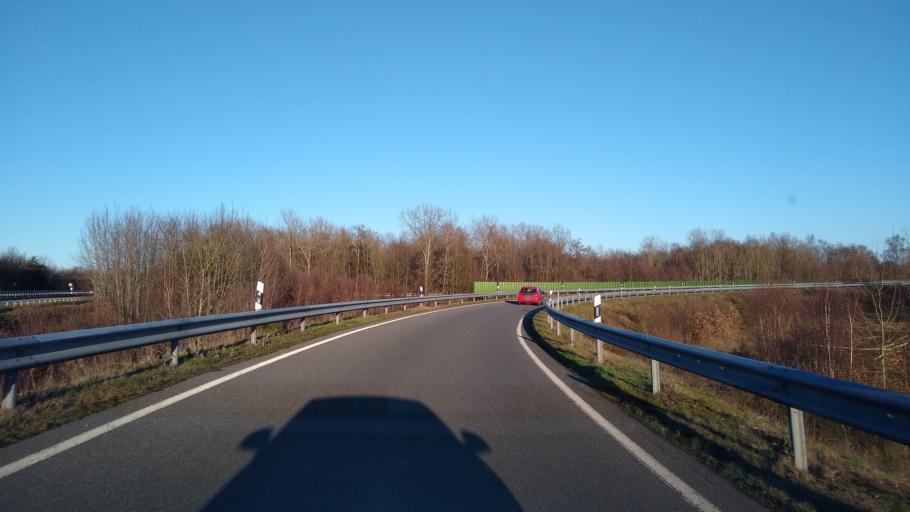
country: DE
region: Lower Saxony
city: Rastede
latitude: 53.2069
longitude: 8.2220
